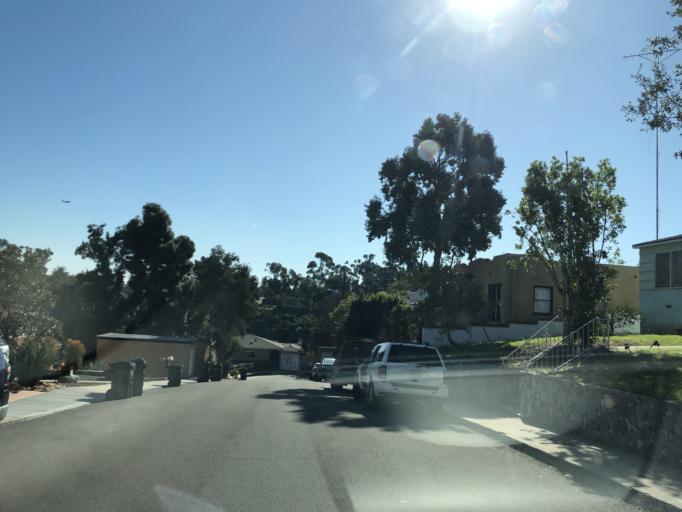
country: US
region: California
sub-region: San Diego County
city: San Diego
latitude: 32.7345
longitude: -117.1304
